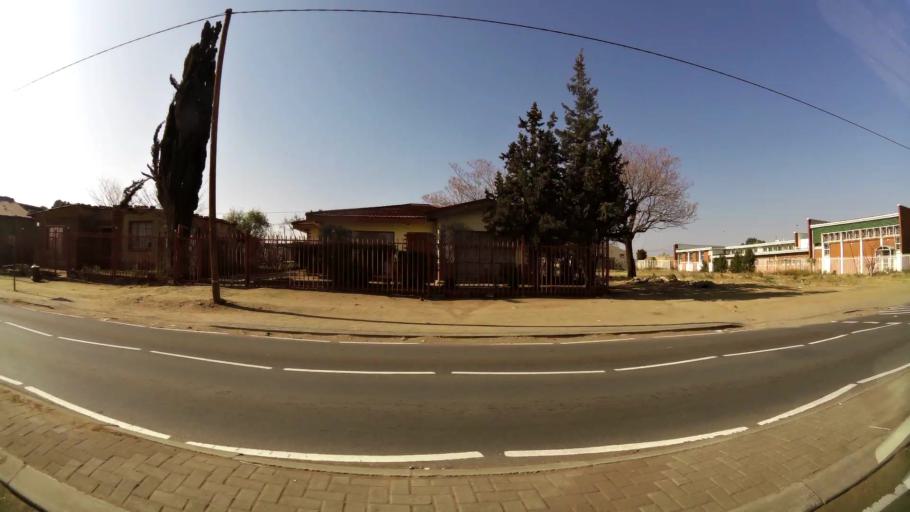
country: ZA
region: Orange Free State
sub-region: Mangaung Metropolitan Municipality
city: Bloemfontein
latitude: -29.1610
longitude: 26.2392
